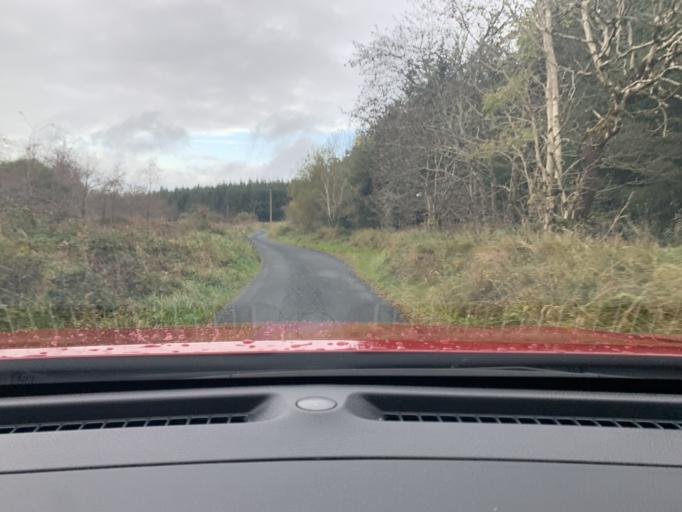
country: IE
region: Connaught
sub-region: Roscommon
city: Ballaghaderreen
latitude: 53.9725
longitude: -8.5990
